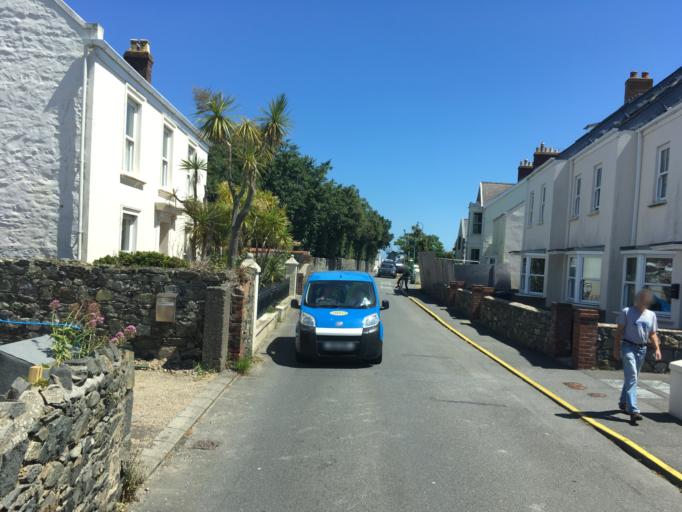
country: GG
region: St Peter Port
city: Saint Peter Port
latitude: 49.4807
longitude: -2.5187
